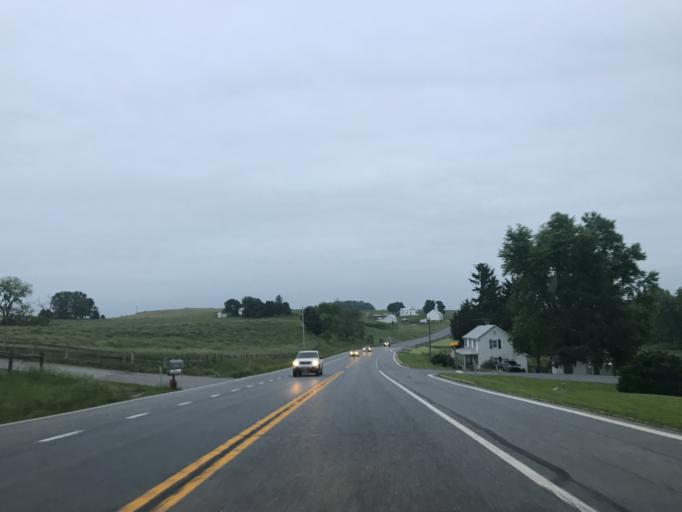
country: US
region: Maryland
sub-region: Frederick County
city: Linganore
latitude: 39.4661
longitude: -77.2483
